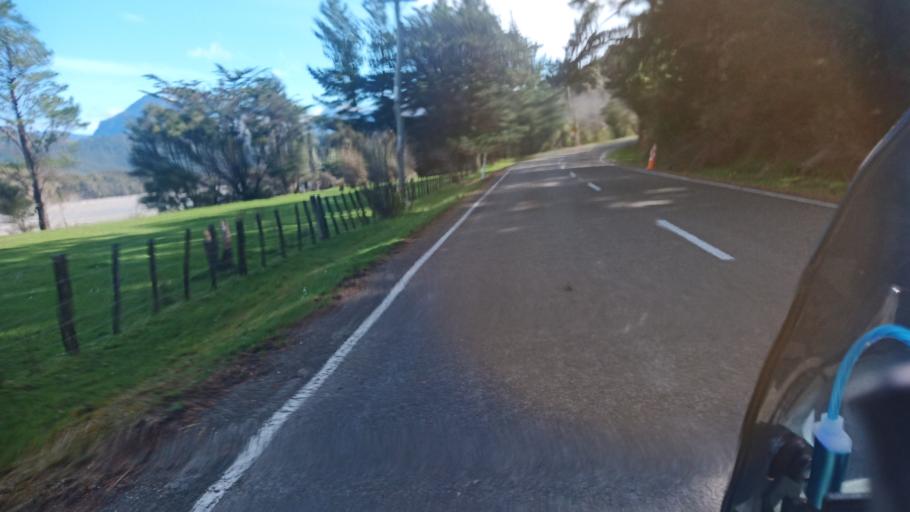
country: NZ
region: Gisborne
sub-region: Gisborne District
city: Gisborne
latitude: -37.8646
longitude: 178.1939
